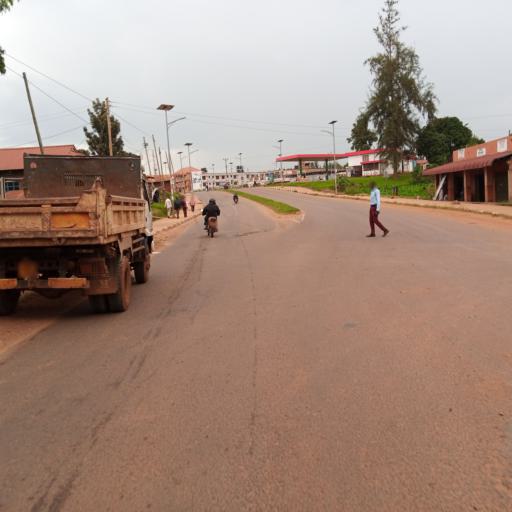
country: UG
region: Eastern Region
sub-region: Mbale District
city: Mbale
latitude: 1.0849
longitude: 34.1777
